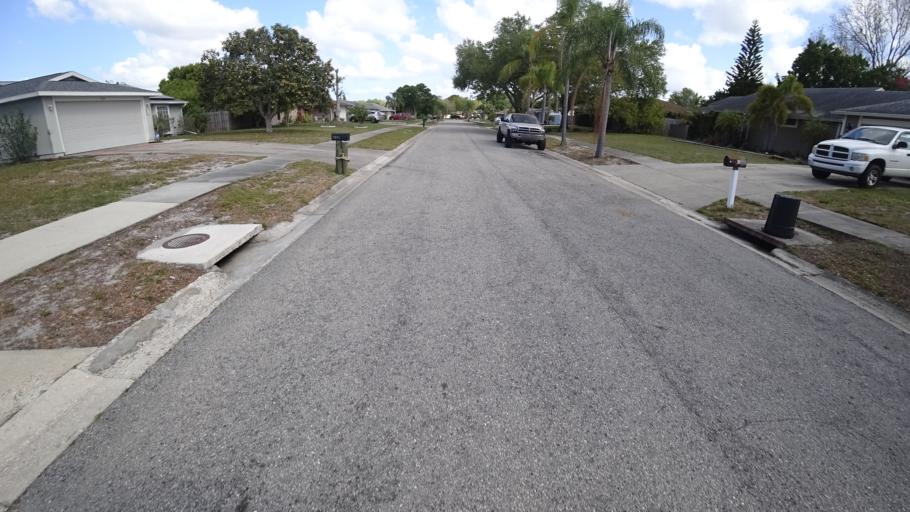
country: US
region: Florida
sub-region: Manatee County
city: Whitfield
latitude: 27.4106
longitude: -82.5613
